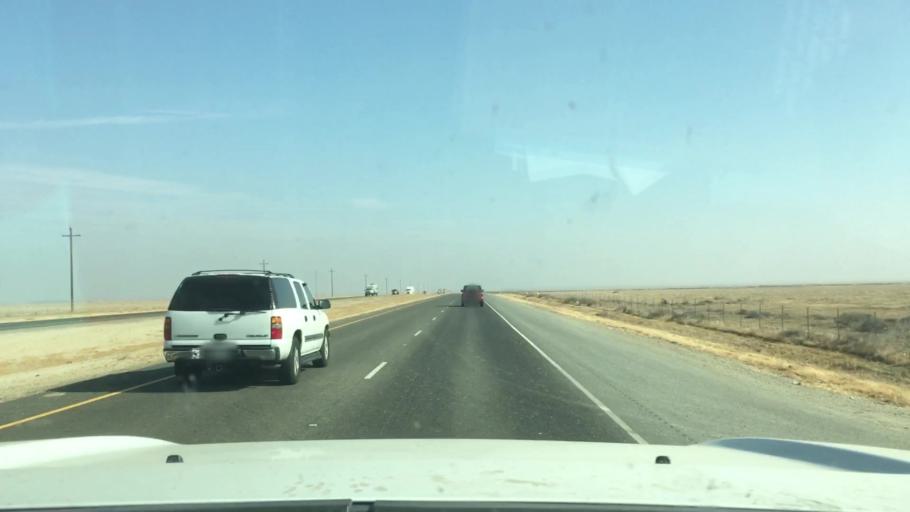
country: US
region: California
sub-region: Kern County
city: Lost Hills
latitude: 35.6152
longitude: -119.8408
